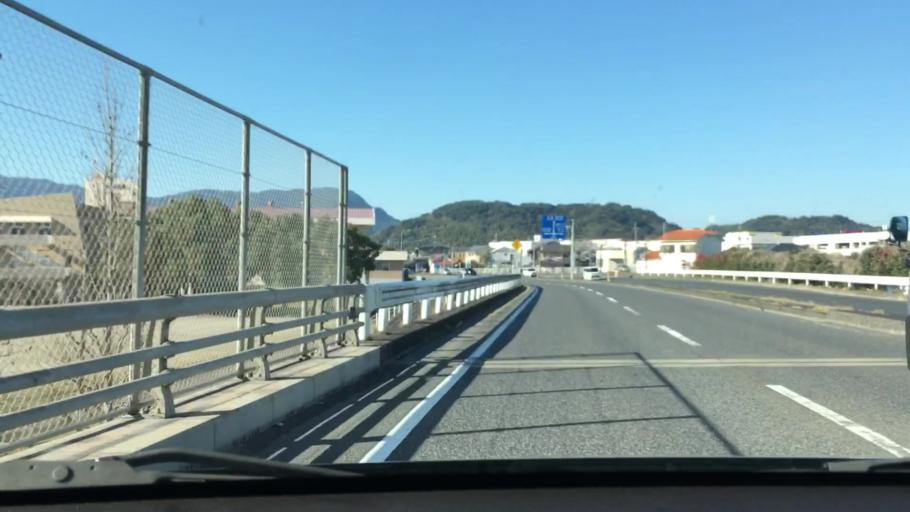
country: JP
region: Kagoshima
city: Kajiki
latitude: 31.7322
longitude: 130.6316
